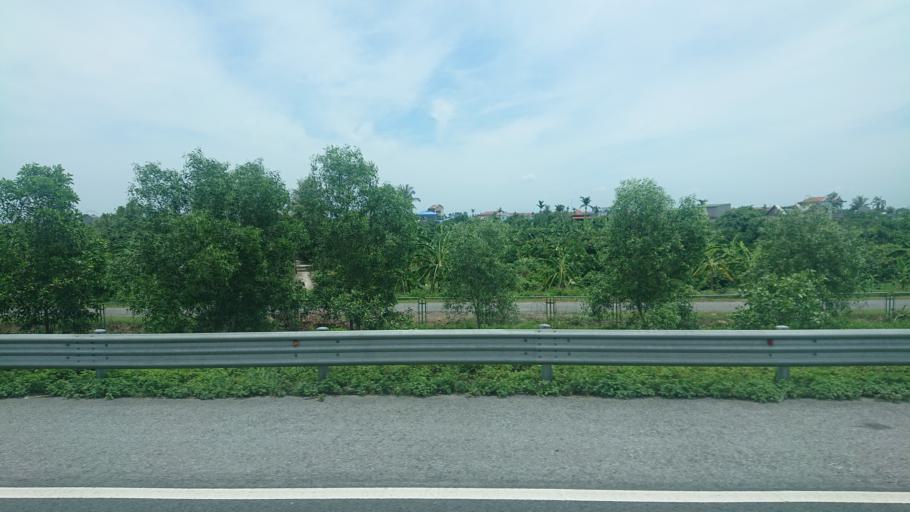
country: VN
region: Hai Duong
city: Tu Ky
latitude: 20.8280
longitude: 106.4564
